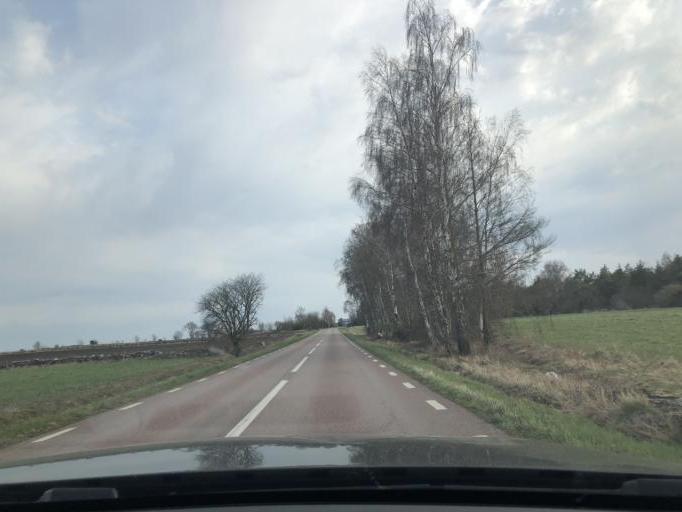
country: SE
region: Kalmar
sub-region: Morbylanga Kommun
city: Sodra Sandby
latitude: 56.5609
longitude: 16.6206
